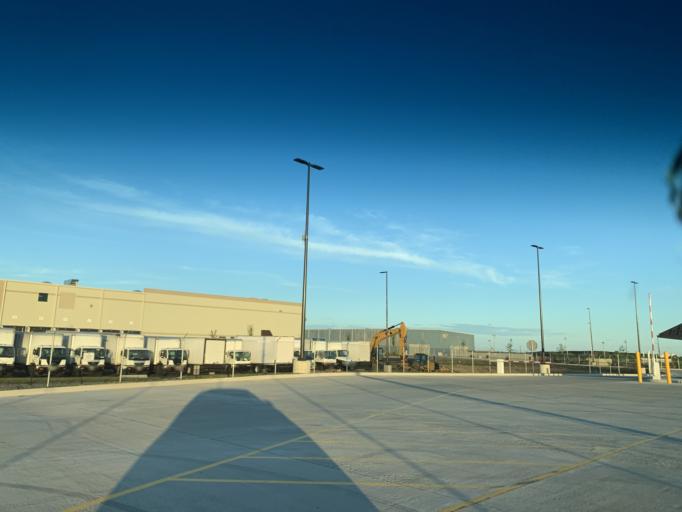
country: US
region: Maryland
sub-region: Baltimore County
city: Edgemere
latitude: 39.2165
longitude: -76.4848
